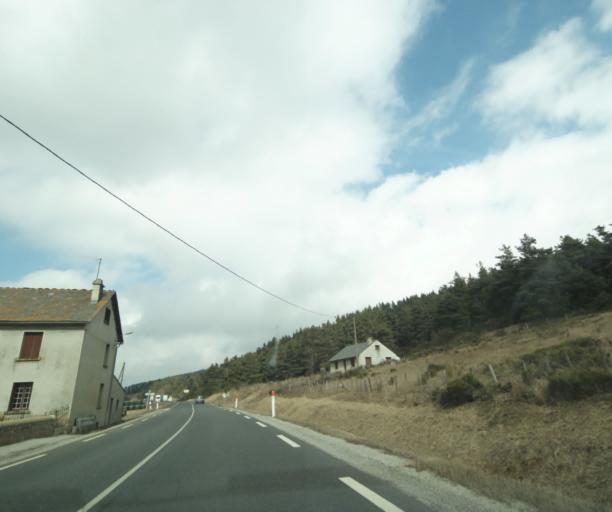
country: FR
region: Languedoc-Roussillon
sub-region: Departement de la Lozere
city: Mende
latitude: 44.6063
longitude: 3.6755
